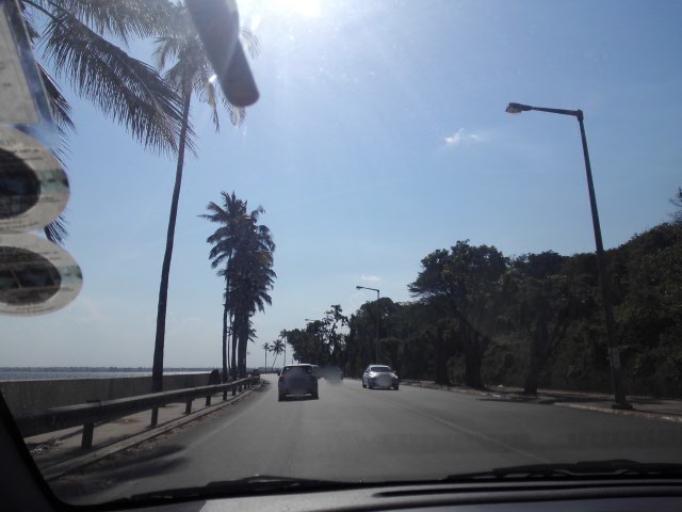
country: MZ
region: Maputo City
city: Maputo
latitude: -25.9838
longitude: 32.5913
